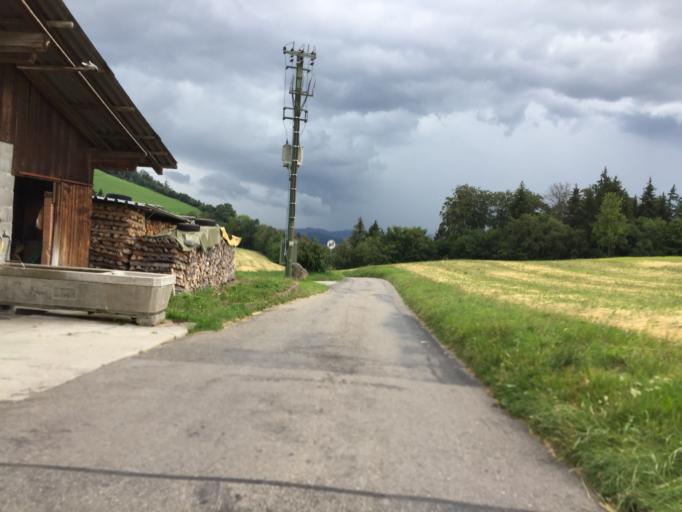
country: CH
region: Bern
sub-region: Bern-Mittelland District
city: Munsingen
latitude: 46.8625
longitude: 7.5453
